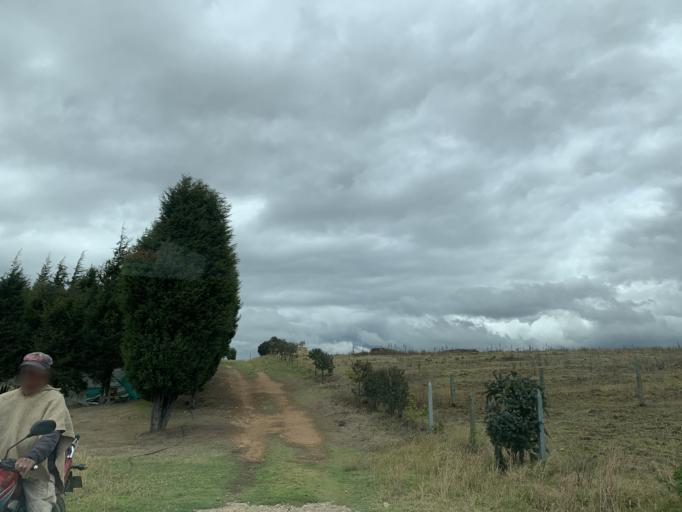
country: CO
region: Boyaca
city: Tunja
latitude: 5.5598
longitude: -73.3140
